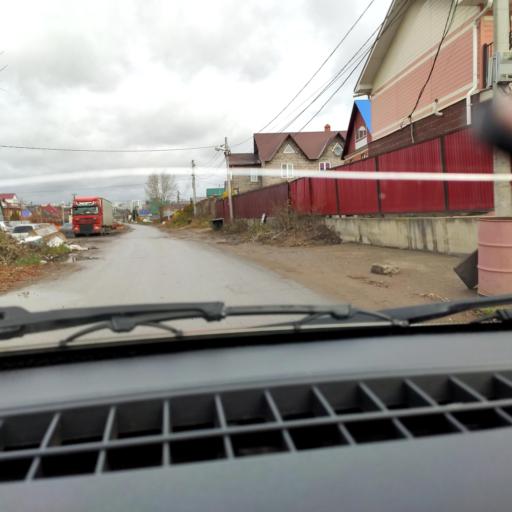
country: RU
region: Bashkortostan
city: Ufa
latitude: 54.6949
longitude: 55.9542
